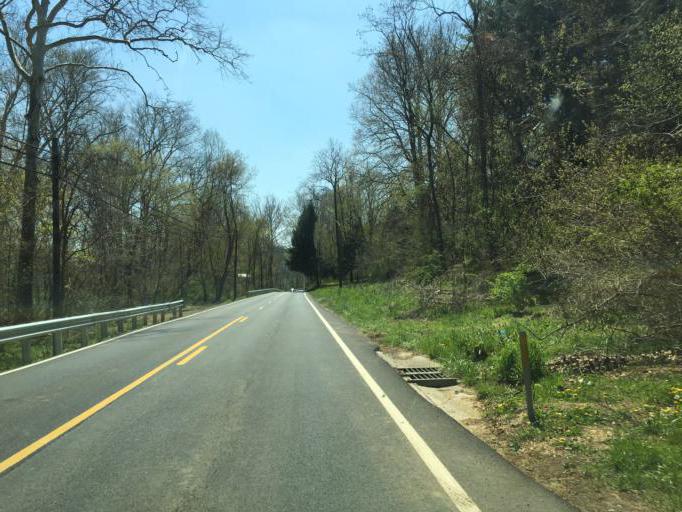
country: US
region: Maryland
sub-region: Frederick County
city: Myersville
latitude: 39.5330
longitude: -77.5336
